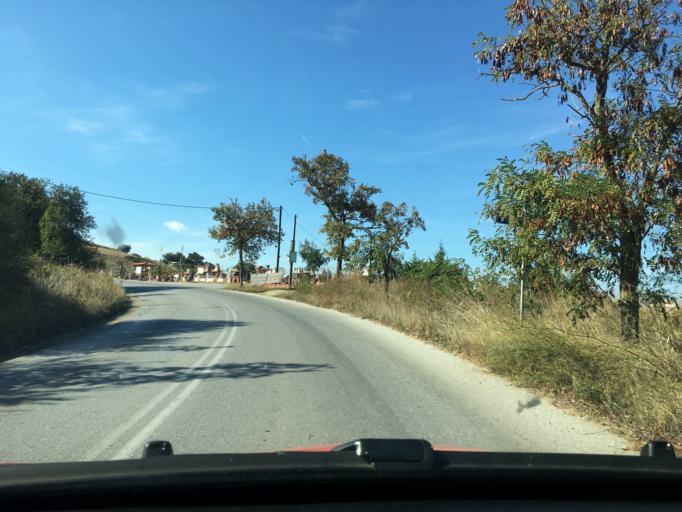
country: GR
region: Central Macedonia
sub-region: Nomos Chalkidikis
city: Nea Roda
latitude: 40.3804
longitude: 23.9200
